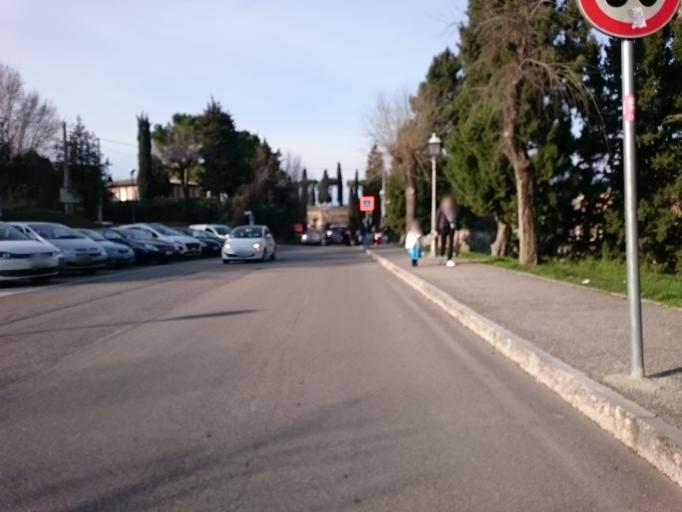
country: IT
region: Veneto
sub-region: Provincia di Verona
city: Peschiera del Garda
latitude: 45.4368
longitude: 10.6916
